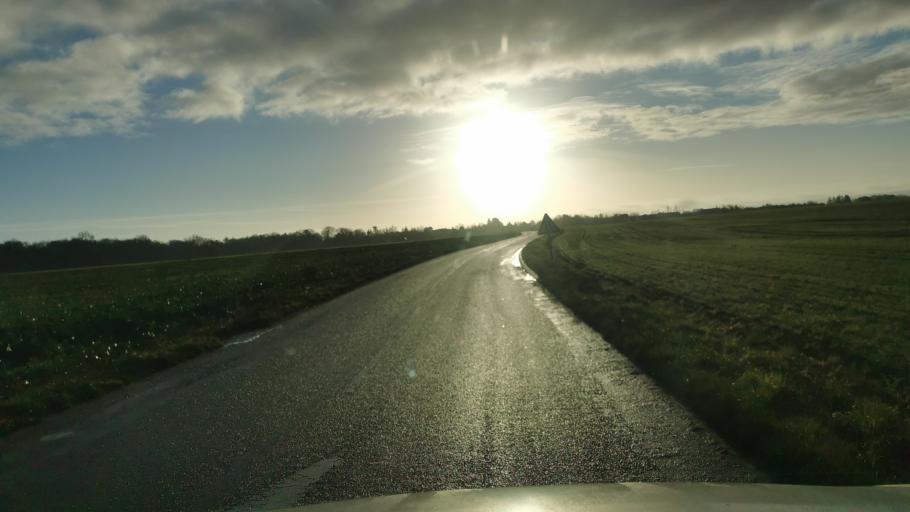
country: FR
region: Ile-de-France
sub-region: Departement des Yvelines
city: Houdan
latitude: 48.8307
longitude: 1.6259
